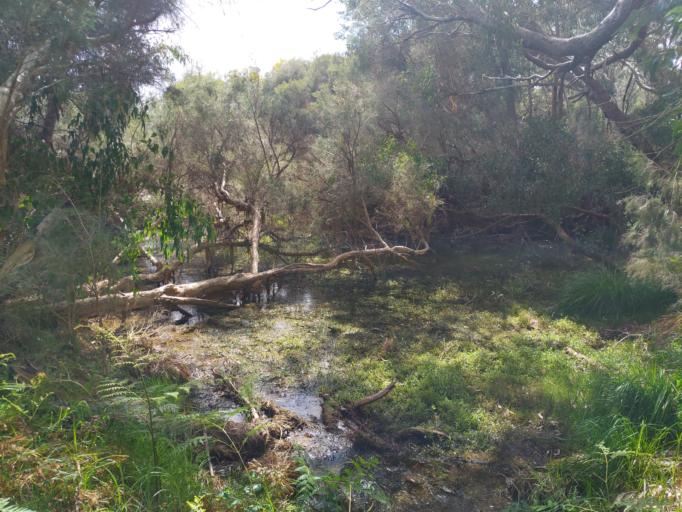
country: AU
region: Western Australia
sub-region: Wanneroo
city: Yanchep
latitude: -31.5483
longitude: 115.6818
